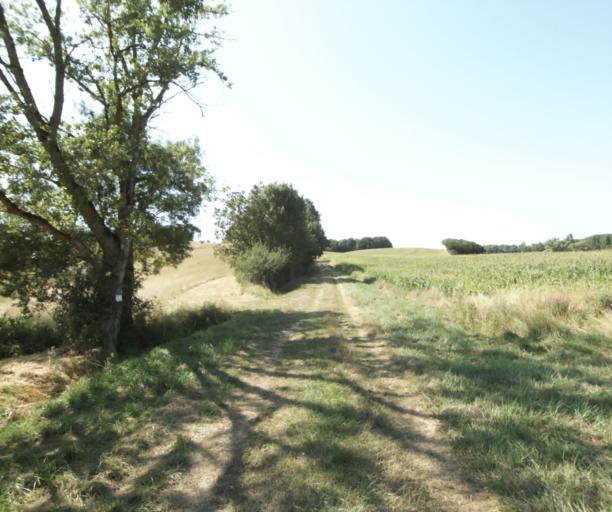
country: FR
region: Midi-Pyrenees
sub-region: Departement de la Haute-Garonne
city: Saint-Felix-Lauragais
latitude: 43.4555
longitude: 1.8609
